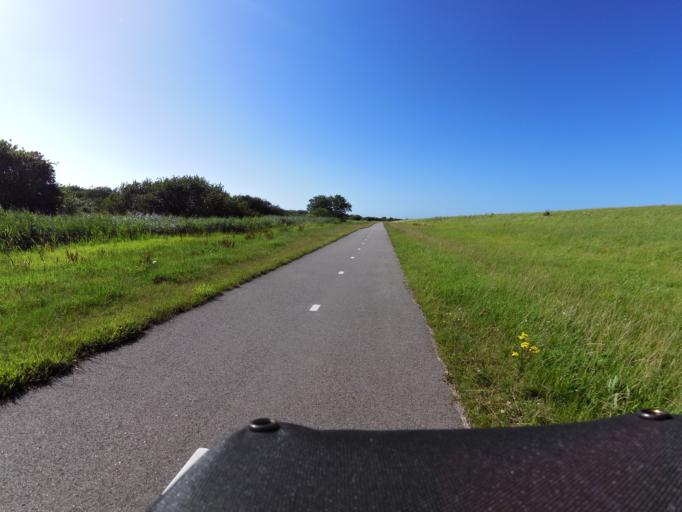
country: NL
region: South Holland
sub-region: Gemeente Goeree-Overflakkee
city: Goedereede
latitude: 51.7883
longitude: 4.0268
